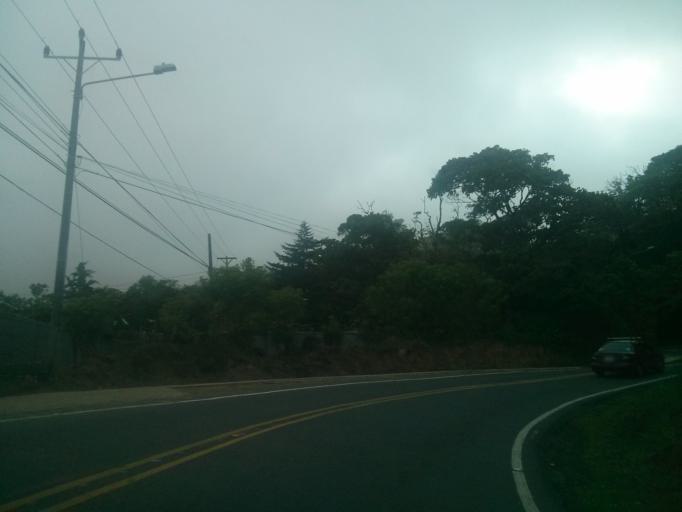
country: CR
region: Cartago
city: Cot
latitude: 9.9116
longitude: -83.8125
